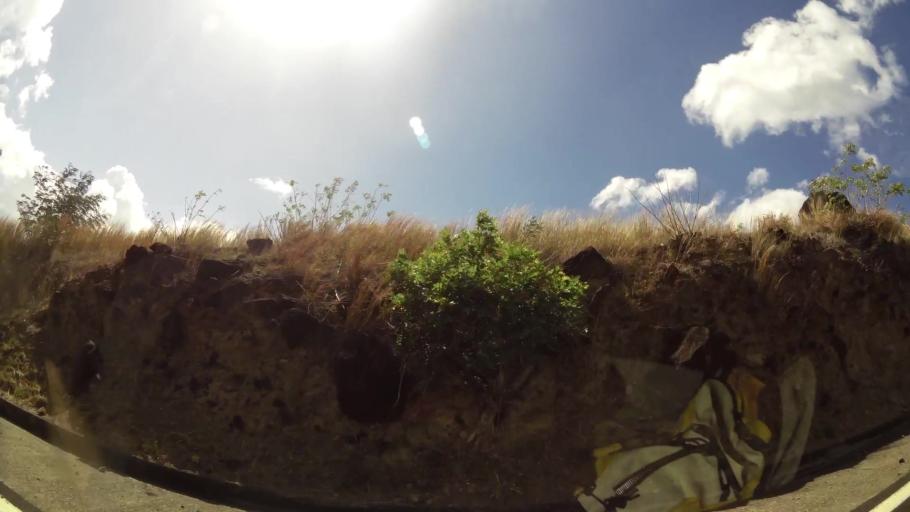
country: MQ
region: Martinique
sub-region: Martinique
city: Saint-Pierre
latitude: 14.6797
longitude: -61.1686
